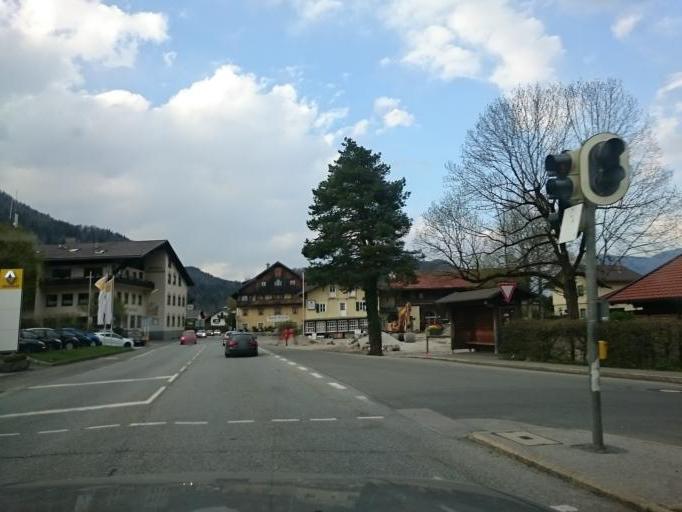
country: DE
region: Bavaria
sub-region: Upper Bavaria
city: Oberau
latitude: 47.5590
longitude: 11.1381
